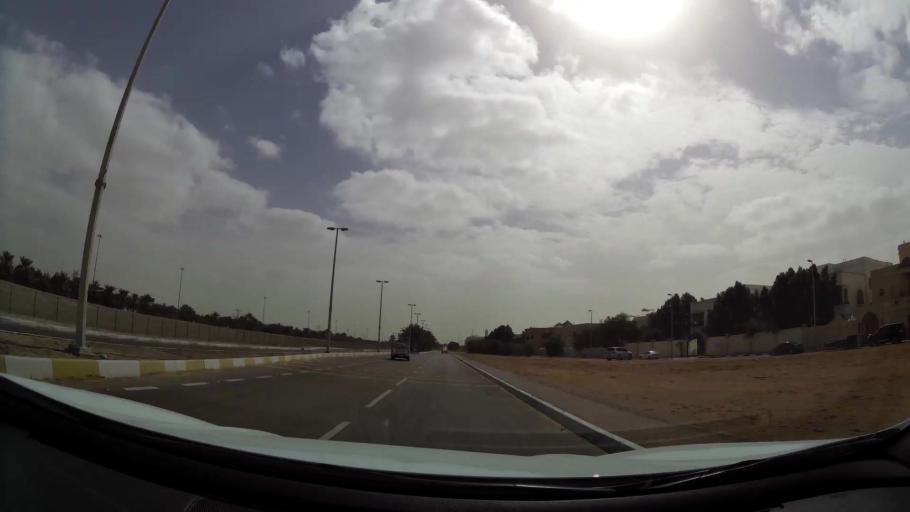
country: AE
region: Abu Dhabi
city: Abu Dhabi
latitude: 24.4091
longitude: 54.5126
